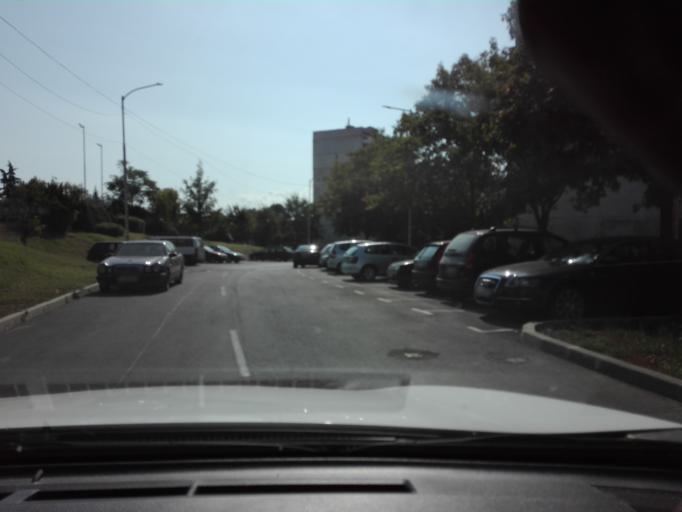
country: BG
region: Burgas
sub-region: Obshtina Burgas
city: Burgas
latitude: 42.4555
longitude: 27.4208
